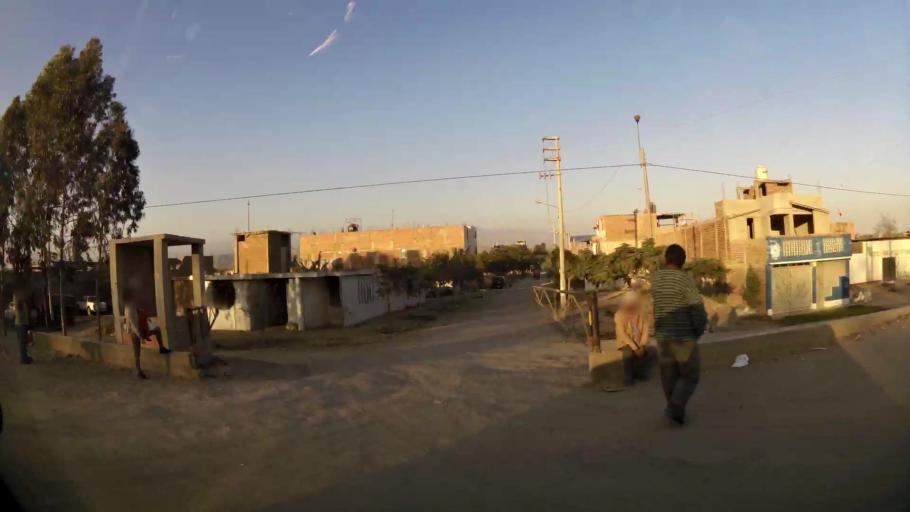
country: PE
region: Ica
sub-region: Provincia de Ica
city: Ica
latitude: -14.0815
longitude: -75.7177
